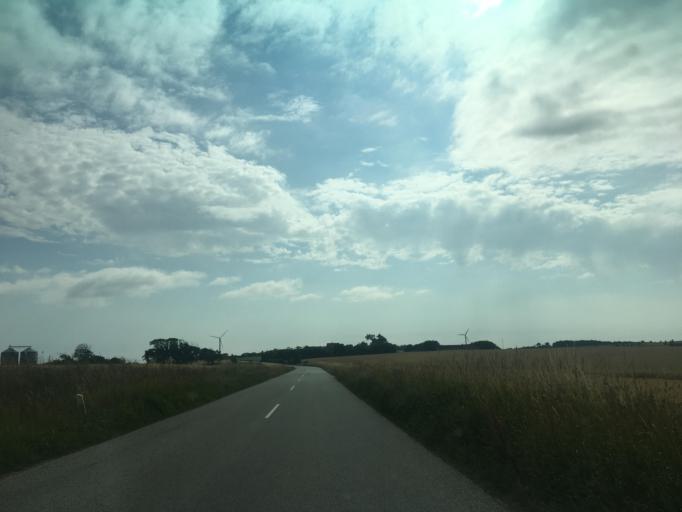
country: DK
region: North Denmark
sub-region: Thisted Kommune
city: Thisted
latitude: 56.8609
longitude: 8.6109
